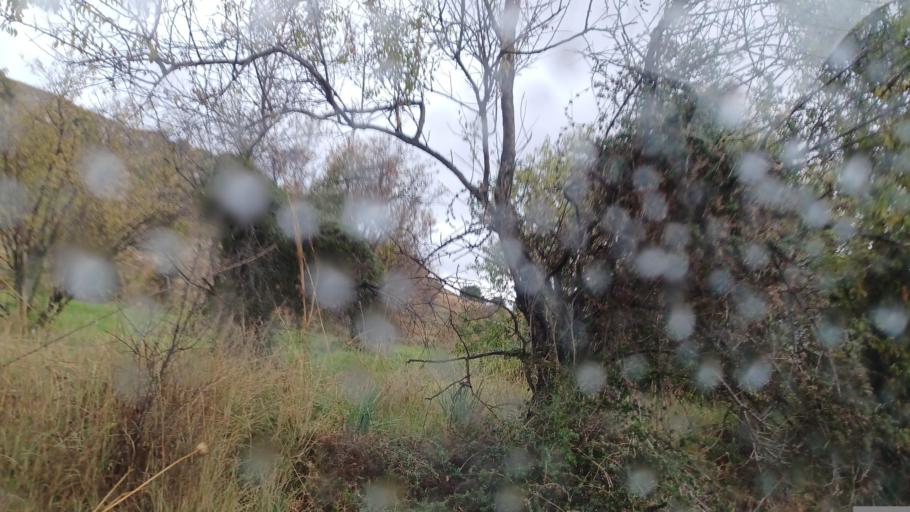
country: CY
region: Pafos
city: Mesogi
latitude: 34.8728
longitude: 32.5441
